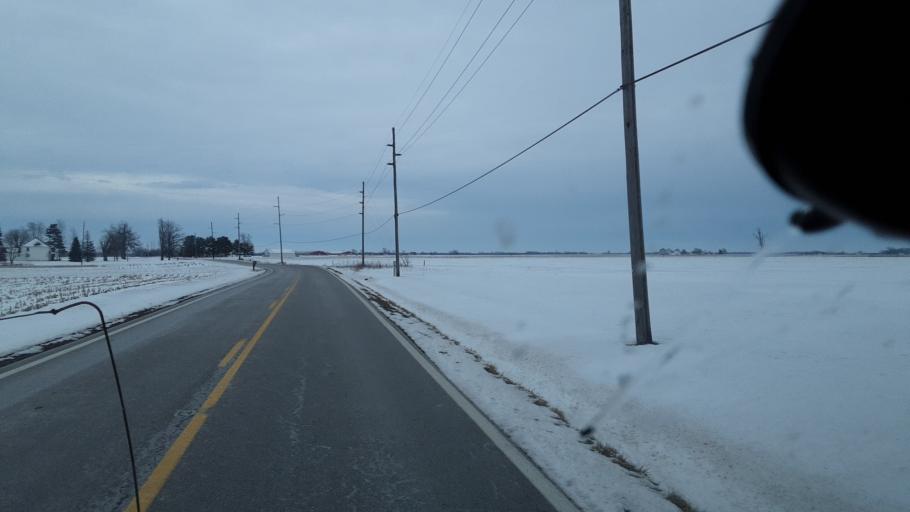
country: US
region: Ohio
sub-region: Madison County
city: Mount Sterling
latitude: 39.6891
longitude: -83.2170
